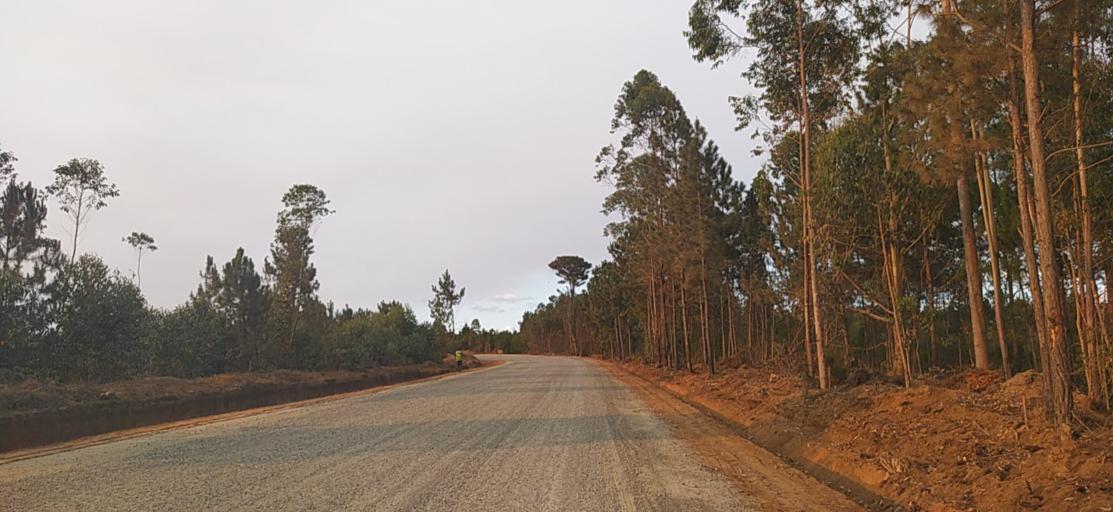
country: MG
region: Alaotra Mangoro
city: Moramanga
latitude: -18.5467
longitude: 48.2597
